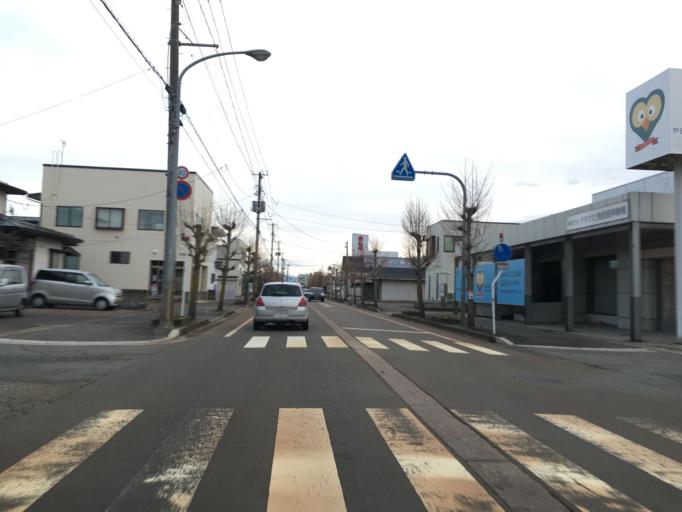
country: JP
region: Yamagata
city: Nagai
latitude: 38.0979
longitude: 140.0363
